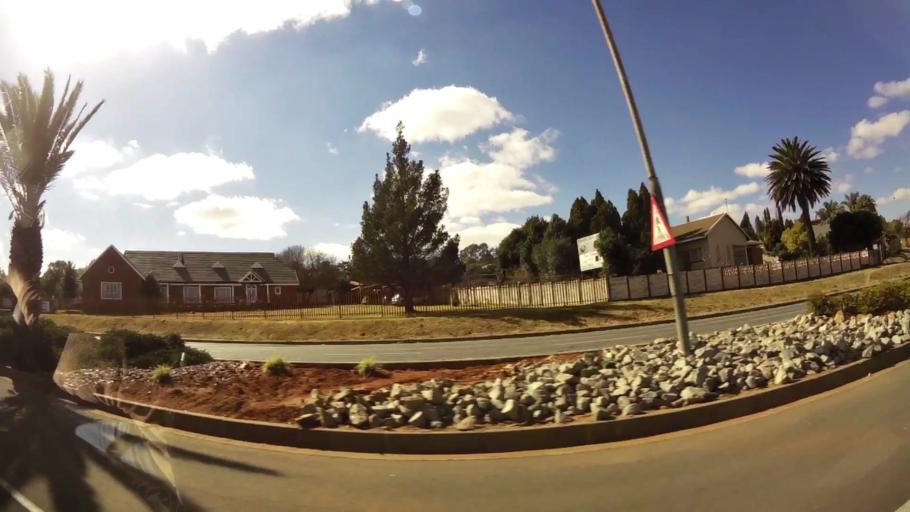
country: ZA
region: Gauteng
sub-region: West Rand District Municipality
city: Krugersdorp
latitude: -26.0972
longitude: 27.7788
